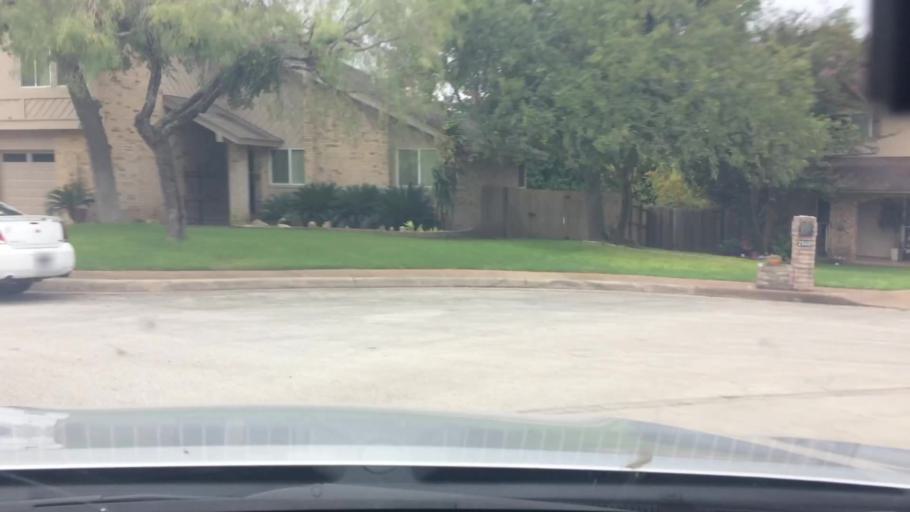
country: US
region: Texas
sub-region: Bexar County
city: Hollywood Park
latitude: 29.5782
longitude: -98.4572
